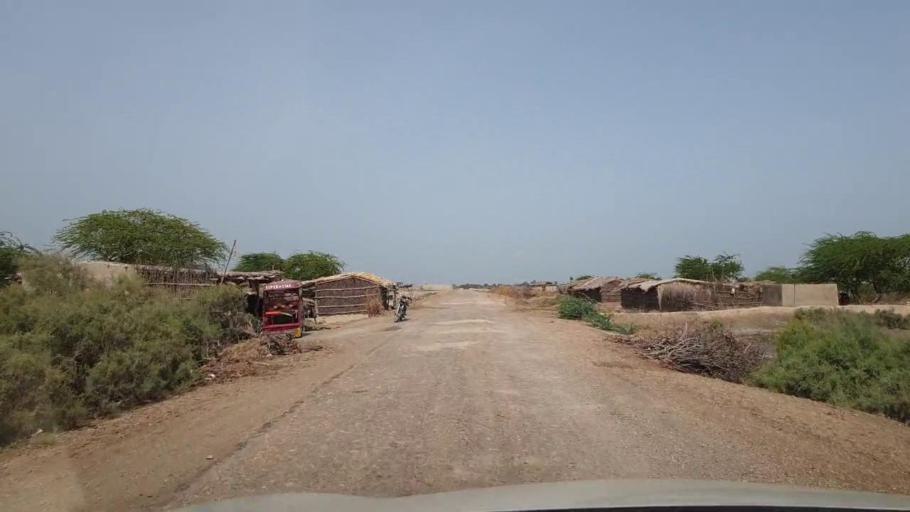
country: PK
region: Sindh
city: Mirwah Gorchani
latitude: 25.2778
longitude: 68.9454
